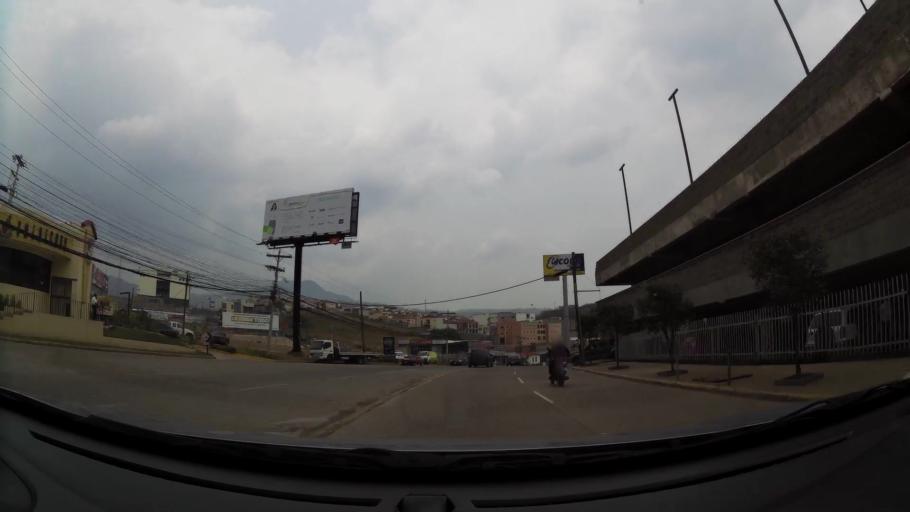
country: HN
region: Francisco Morazan
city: Tegucigalpa
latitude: 14.0822
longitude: -87.1685
